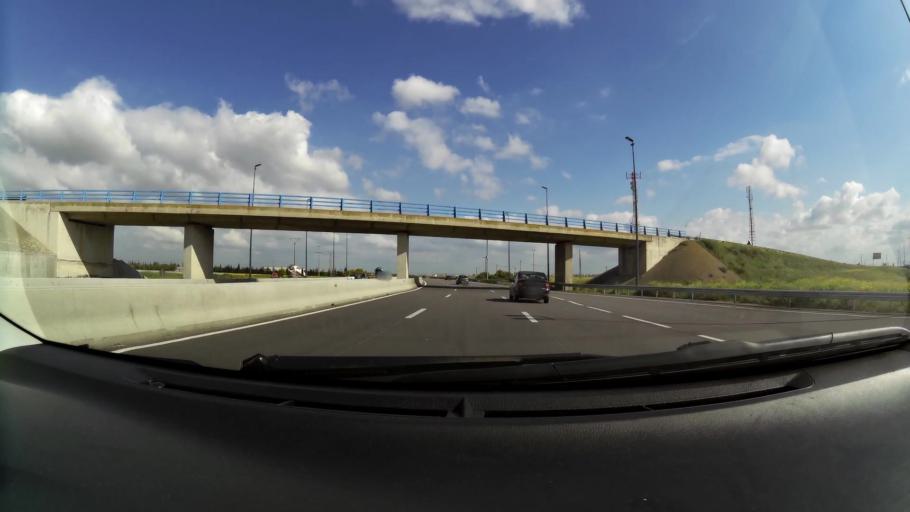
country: MA
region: Chaouia-Ouardigha
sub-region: Settat Province
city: Berrechid
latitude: 33.3173
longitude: -7.6021
